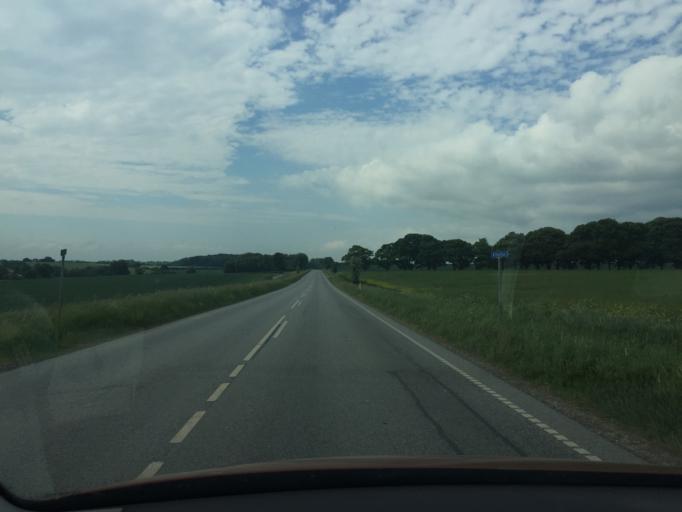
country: DK
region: South Denmark
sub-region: Haderslev Kommune
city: Starup
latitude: 55.2535
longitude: 9.6010
